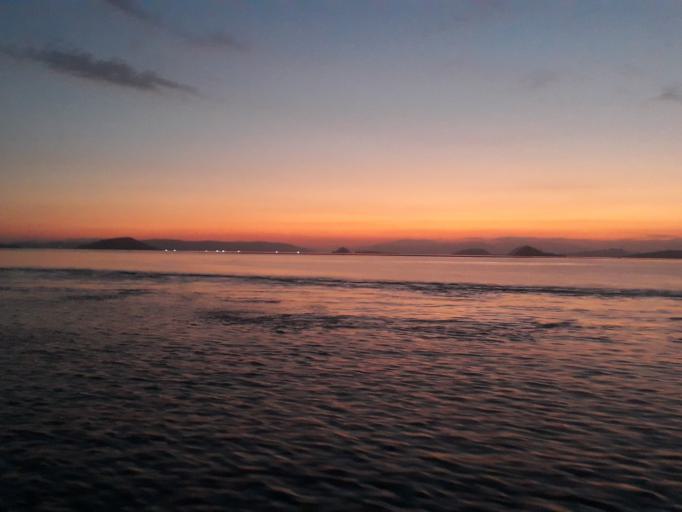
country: ID
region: East Nusa Tenggara
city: Kenari
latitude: -8.6019
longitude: 119.7659
